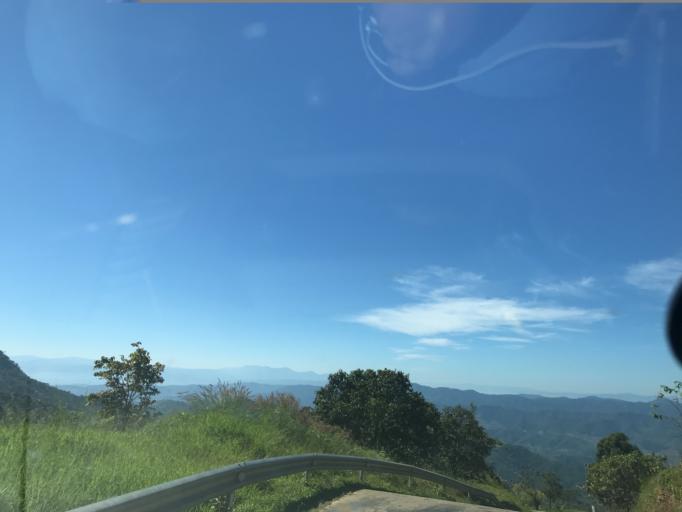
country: TH
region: Chiang Rai
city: Mae Lao
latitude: 19.8193
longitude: 99.5735
